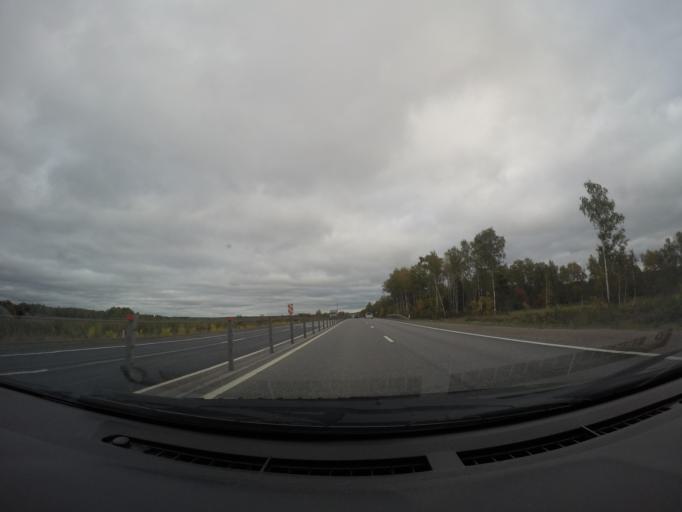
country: RU
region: Moskovskaya
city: Tuchkovo
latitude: 55.5498
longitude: 36.4672
